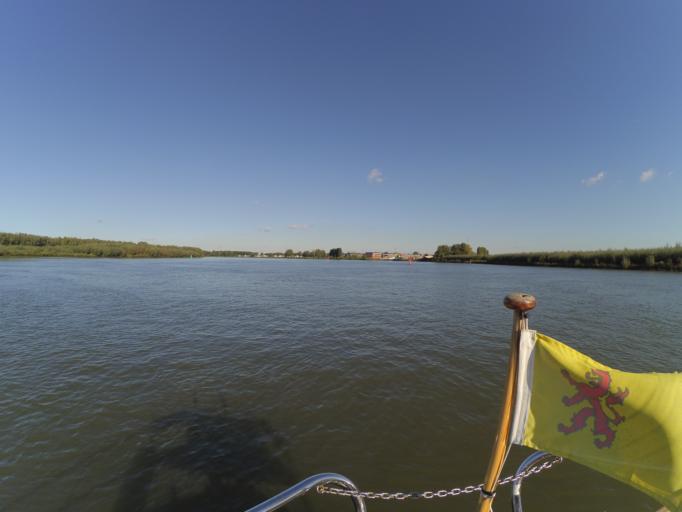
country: NL
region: South Holland
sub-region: Gemeente Zwijndrecht
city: Heerjansdam
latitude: 51.8257
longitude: 4.5588
